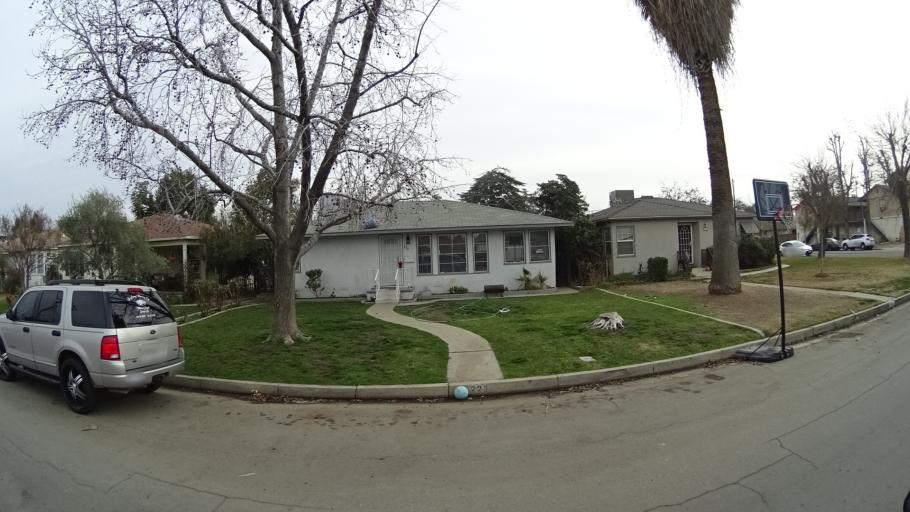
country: US
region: California
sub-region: Kern County
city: Bakersfield
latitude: 35.3584
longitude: -119.0372
